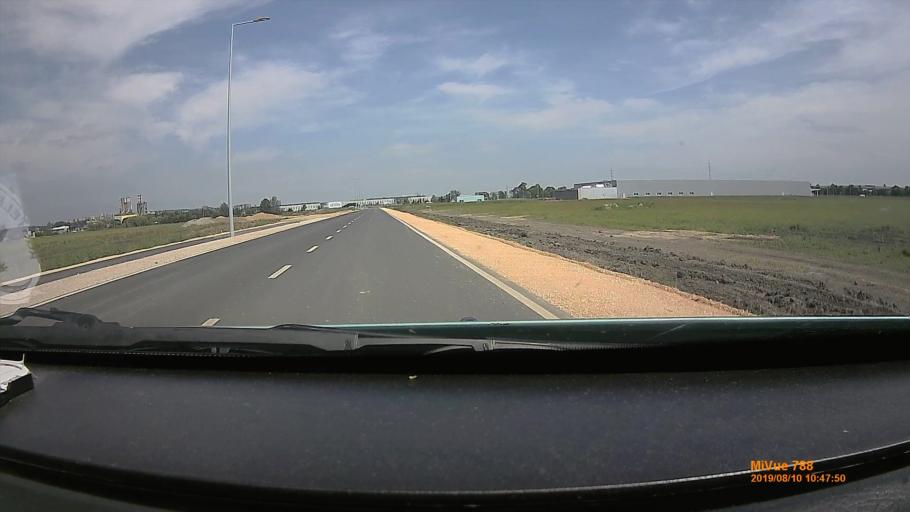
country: HU
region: Borsod-Abauj-Zemplen
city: Malyi
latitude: 48.0510
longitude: 20.8102
